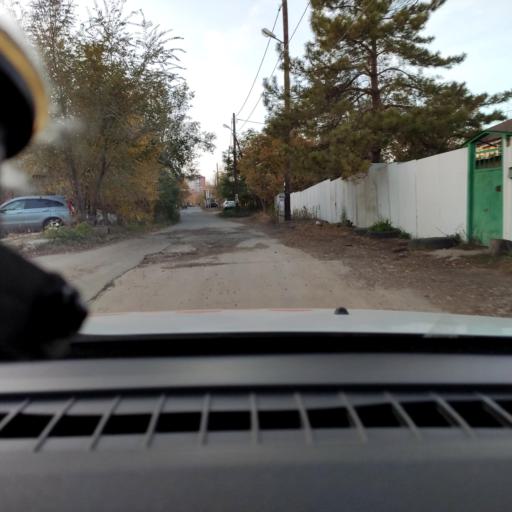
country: RU
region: Samara
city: Samara
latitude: 53.1830
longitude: 50.2085
